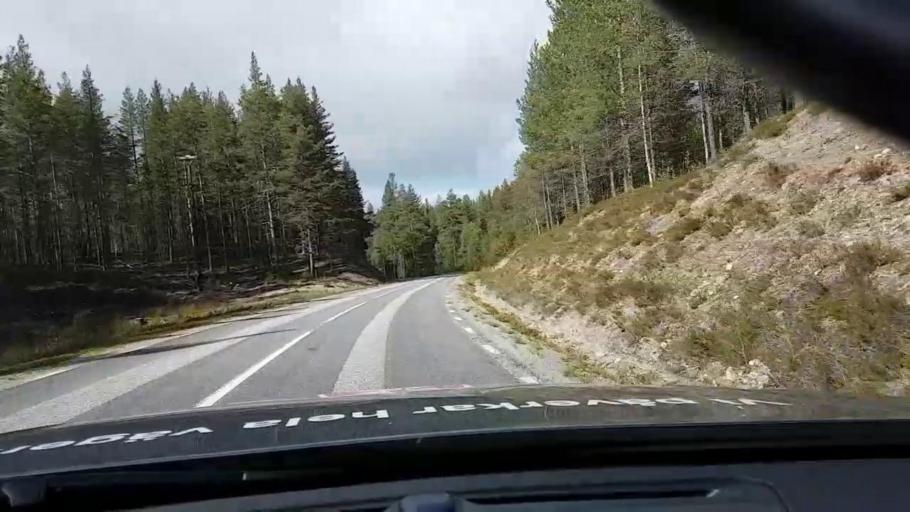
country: SE
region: Vaesterbotten
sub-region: Asele Kommun
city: Asele
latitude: 63.8569
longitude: 17.3852
